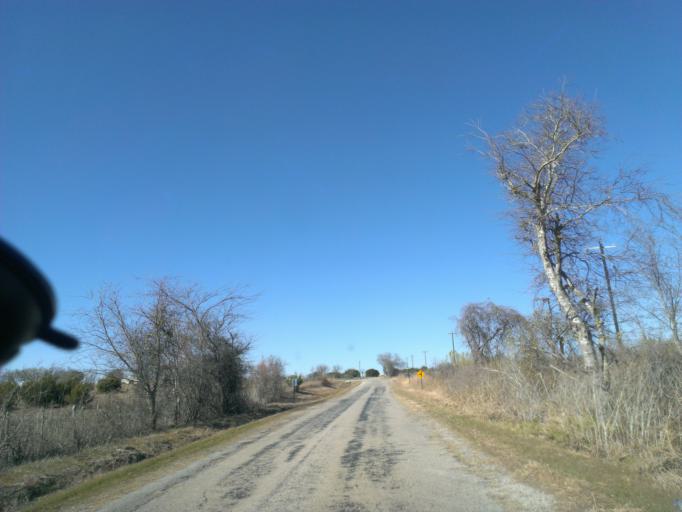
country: US
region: Texas
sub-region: Lampasas County
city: Lampasas
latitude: 30.9483
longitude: -98.1429
